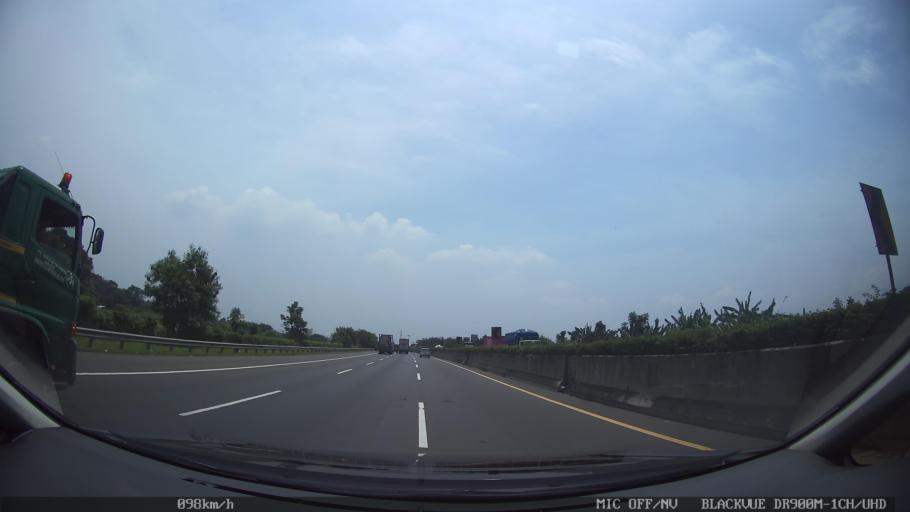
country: ID
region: West Java
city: Kresek
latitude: -6.1773
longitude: 106.3848
